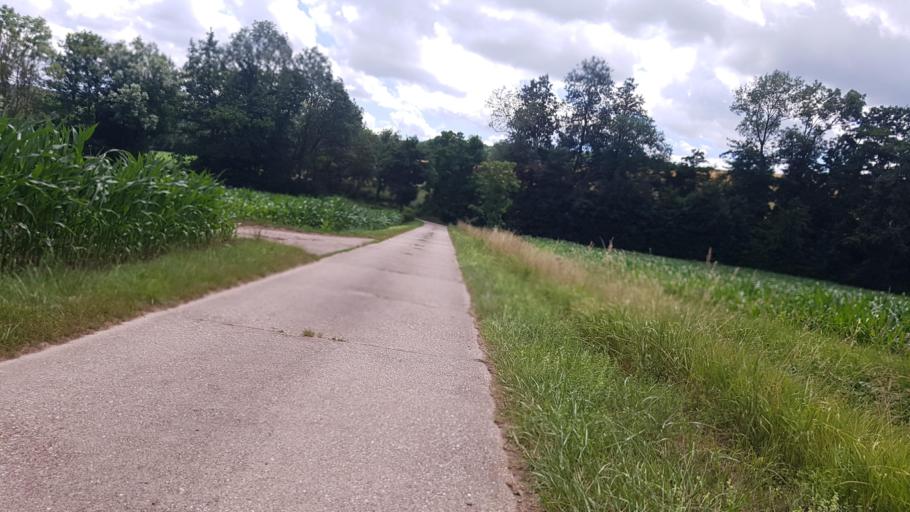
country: DE
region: Baden-Wuerttemberg
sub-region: Karlsruhe Region
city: Zaisenhausen
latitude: 49.1648
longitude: 8.8045
